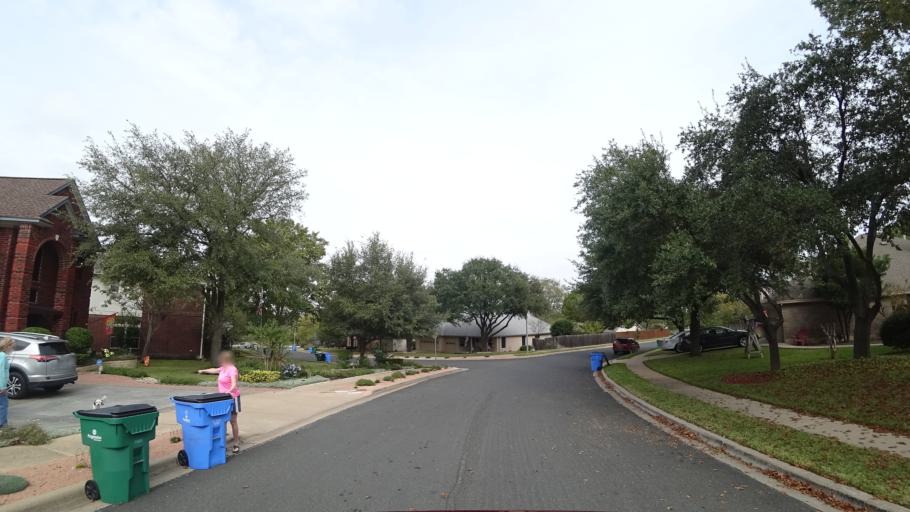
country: US
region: Texas
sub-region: Travis County
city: Wells Branch
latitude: 30.4393
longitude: -97.6795
